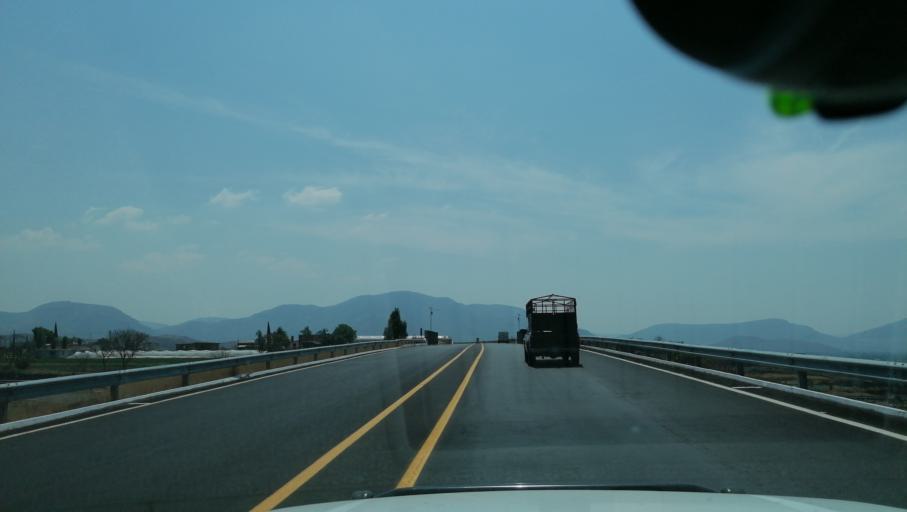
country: MX
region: Puebla
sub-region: Santa Isabel Cholula
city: Santa Ana Acozautla
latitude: 18.9386
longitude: -98.3921
